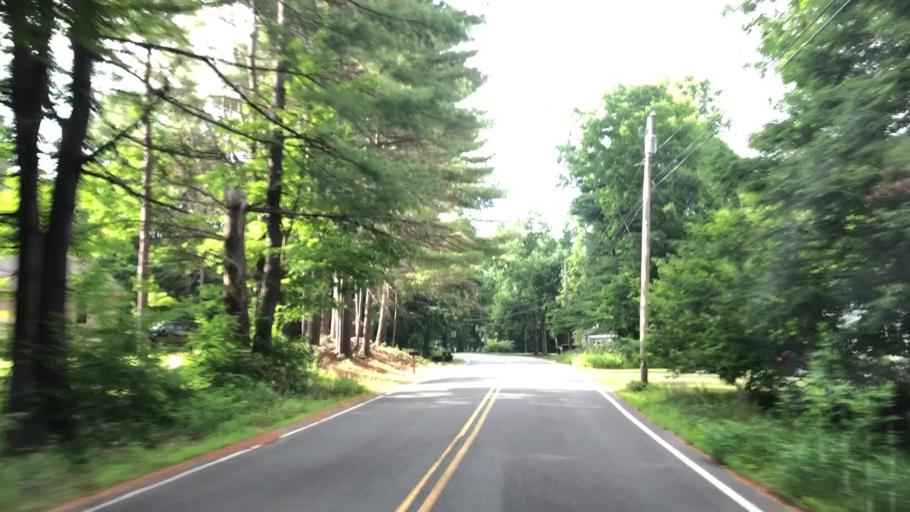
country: US
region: Massachusetts
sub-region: Hampshire County
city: Southampton
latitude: 42.2180
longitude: -72.7460
